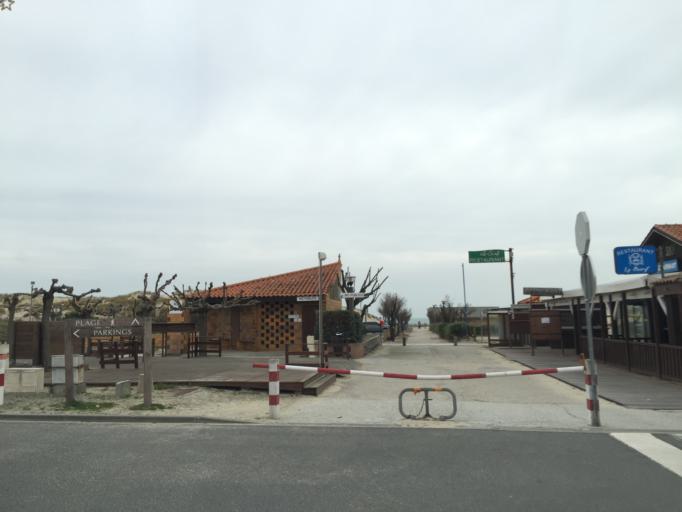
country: FR
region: Aquitaine
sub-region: Departement de la Gironde
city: Hourtin
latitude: 45.2232
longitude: -1.1695
